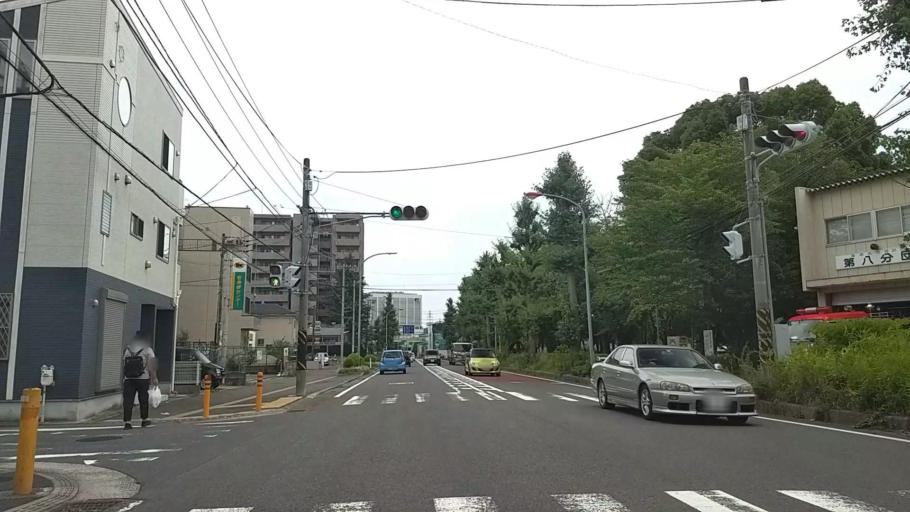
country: JP
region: Kanagawa
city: Minami-rinkan
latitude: 35.4688
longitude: 139.4299
